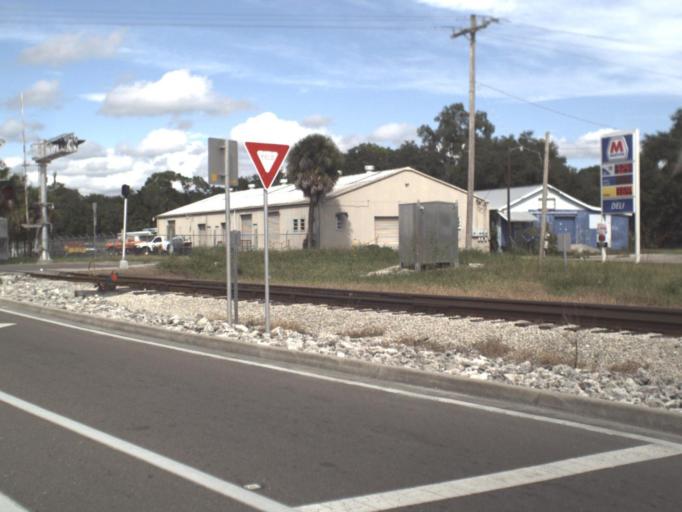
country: US
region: Florida
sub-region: Lee County
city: Fort Myers
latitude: 26.6332
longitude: -81.8603
